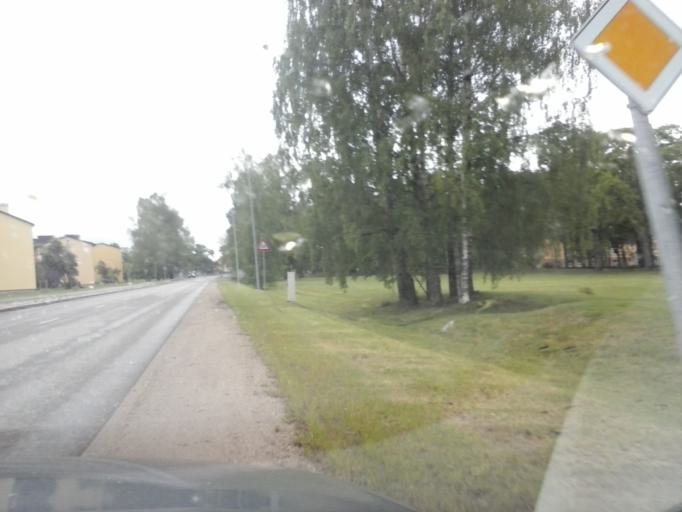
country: LV
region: Valmieras Rajons
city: Valmiera
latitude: 57.5518
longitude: 25.4357
